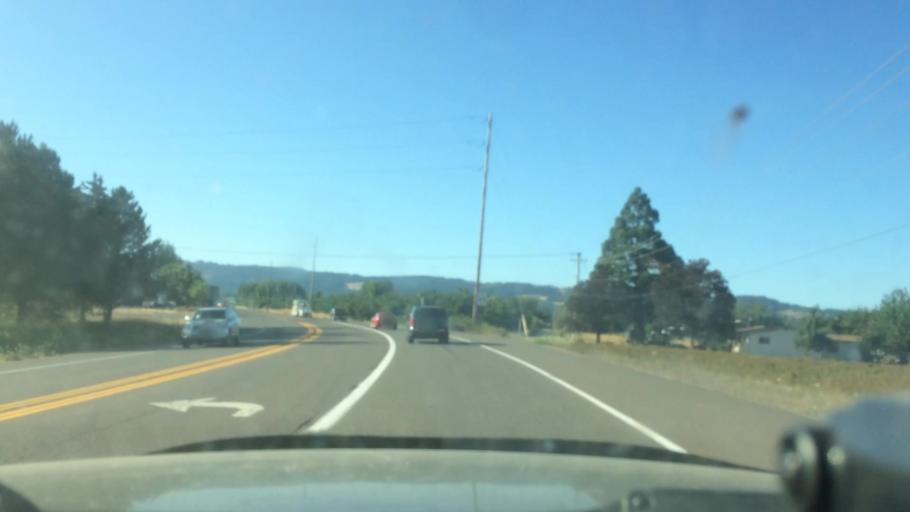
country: US
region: Oregon
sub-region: Yamhill County
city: Newberg
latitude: 45.2853
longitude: -122.9450
